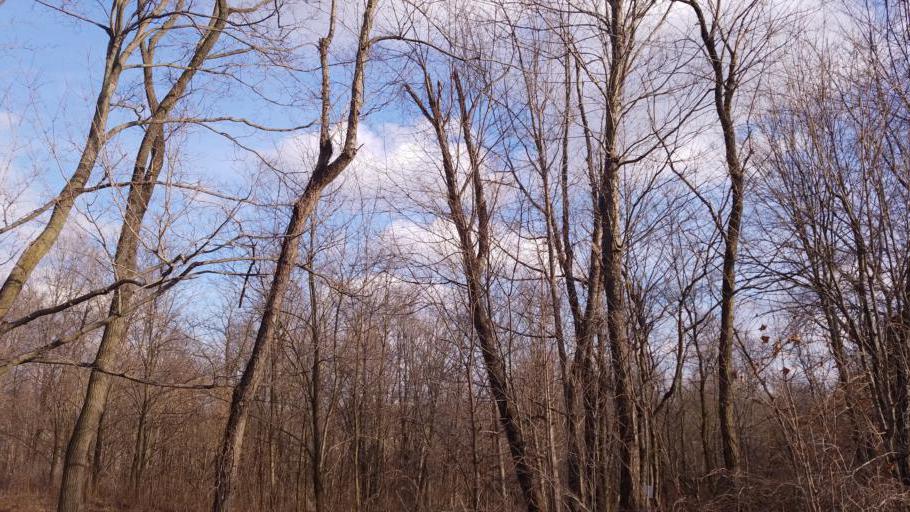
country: US
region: Ohio
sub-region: Crawford County
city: Galion
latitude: 40.7055
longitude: -82.7172
